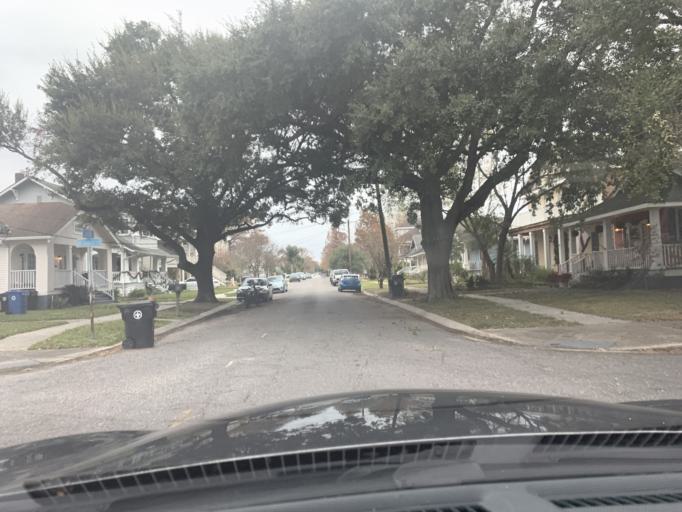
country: US
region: Louisiana
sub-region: Jefferson Parish
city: Metairie
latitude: 29.9973
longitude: -90.1142
